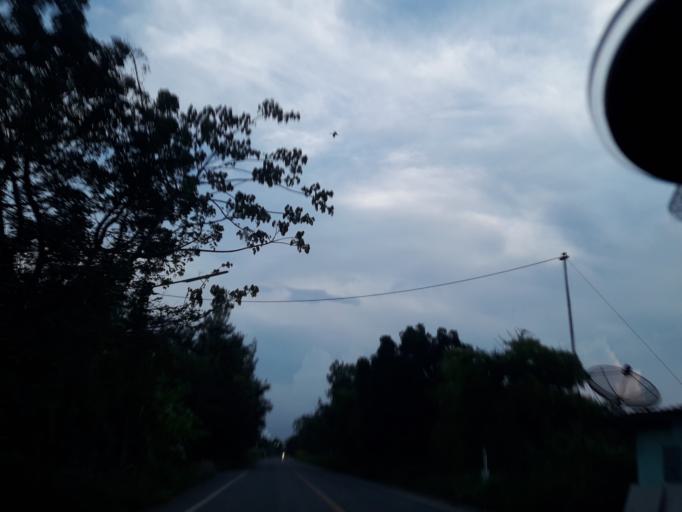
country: TH
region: Pathum Thani
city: Nong Suea
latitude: 14.1245
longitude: 100.8690
